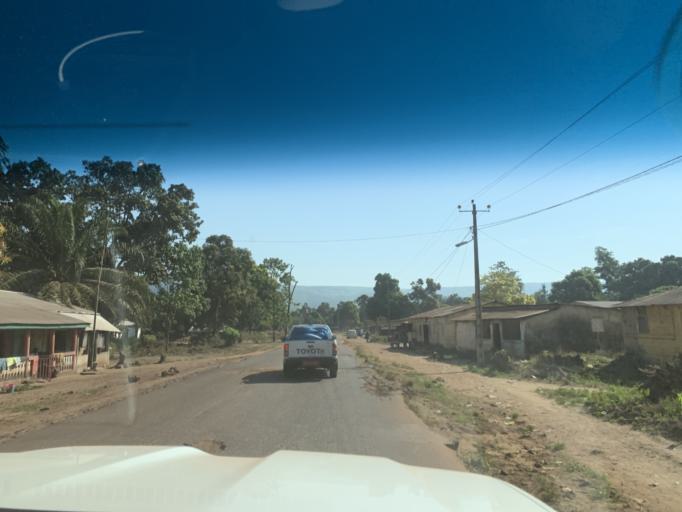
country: GN
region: Kindia
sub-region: Kindia
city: Kindia
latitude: 9.8658
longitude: -13.0598
